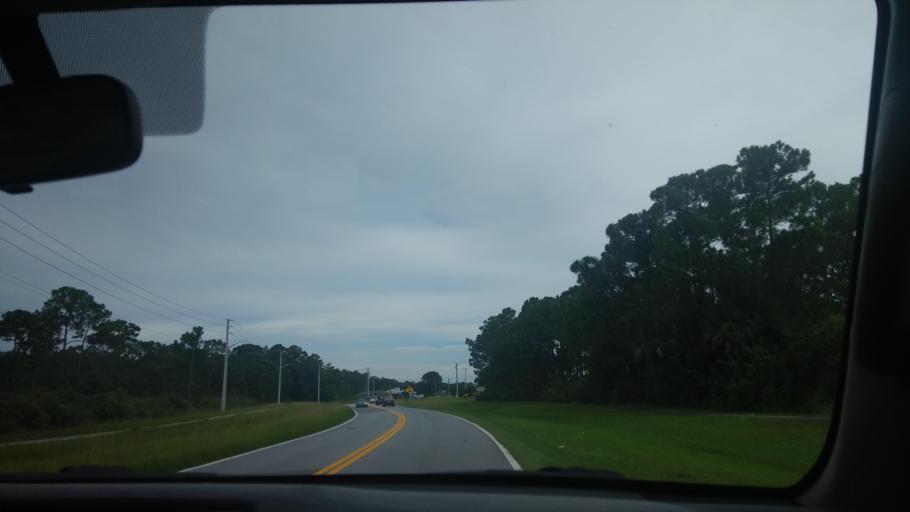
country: US
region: Florida
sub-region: Brevard County
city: Palm Bay
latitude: 27.9838
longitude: -80.6349
